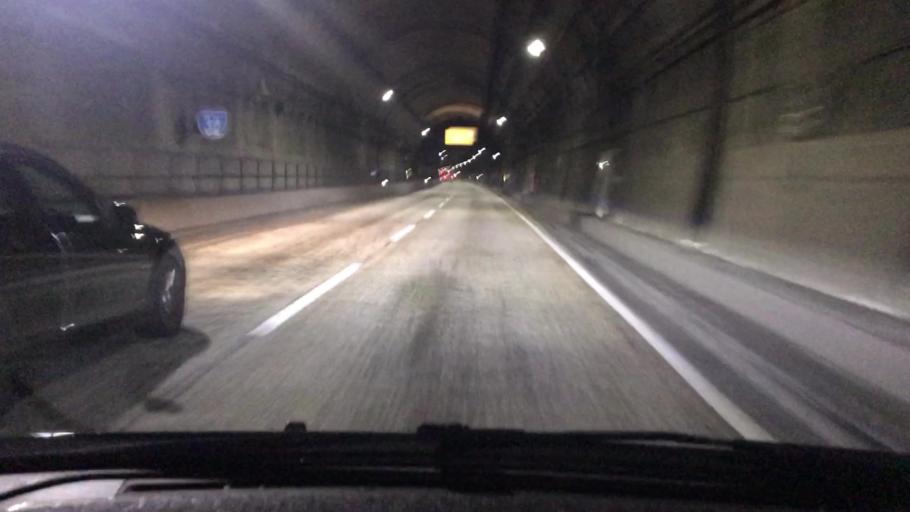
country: JP
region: Hyogo
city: Kobe
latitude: 34.7113
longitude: 135.1917
